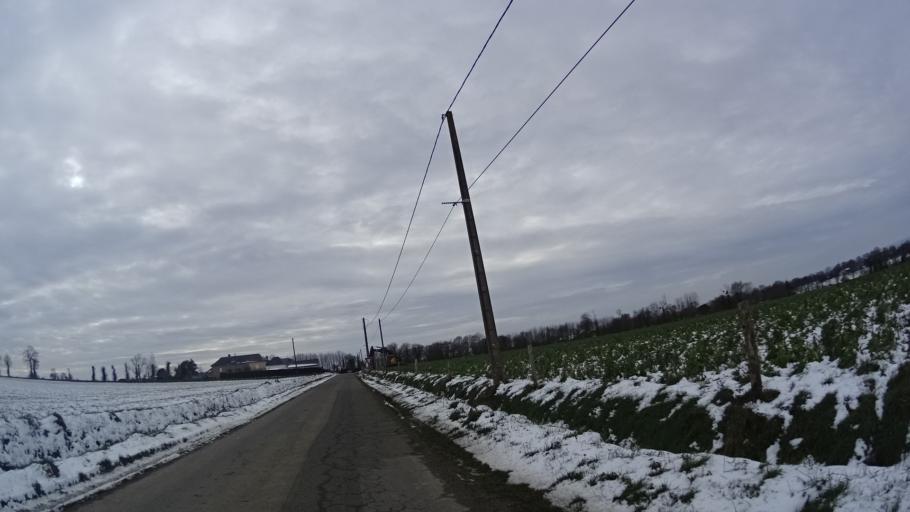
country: FR
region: Brittany
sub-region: Departement des Cotes-d'Armor
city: Plouasne
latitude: 48.3236
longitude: -1.9544
